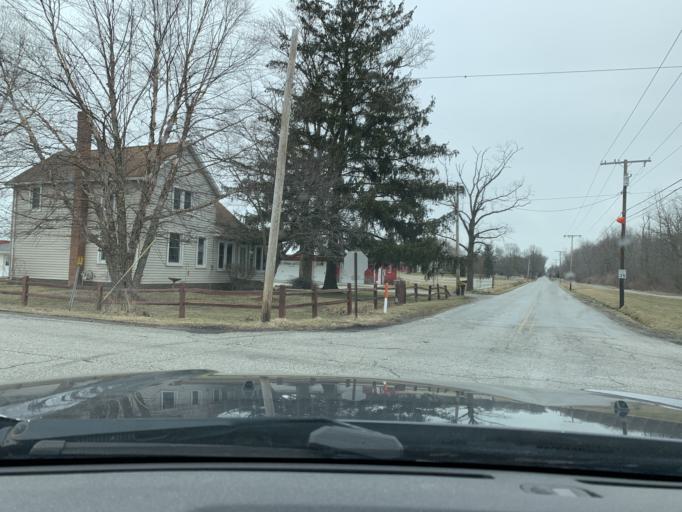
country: US
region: Indiana
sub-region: Porter County
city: Chesterton
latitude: 41.5644
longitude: -87.0665
